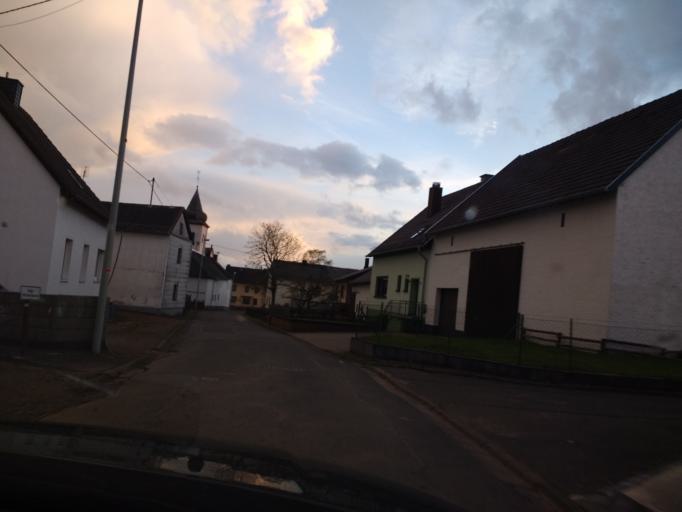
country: DE
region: Rheinland-Pfalz
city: Wiesbaum
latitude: 50.3406
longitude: 6.6715
